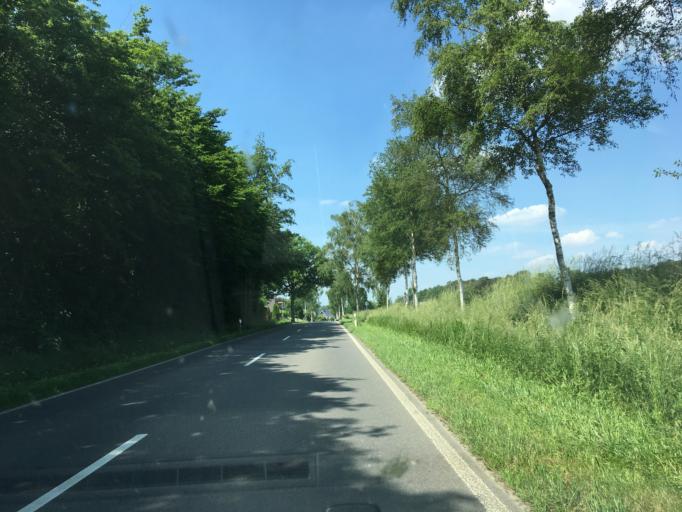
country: DE
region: North Rhine-Westphalia
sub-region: Regierungsbezirk Munster
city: Borken
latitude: 51.8411
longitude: 6.7803
